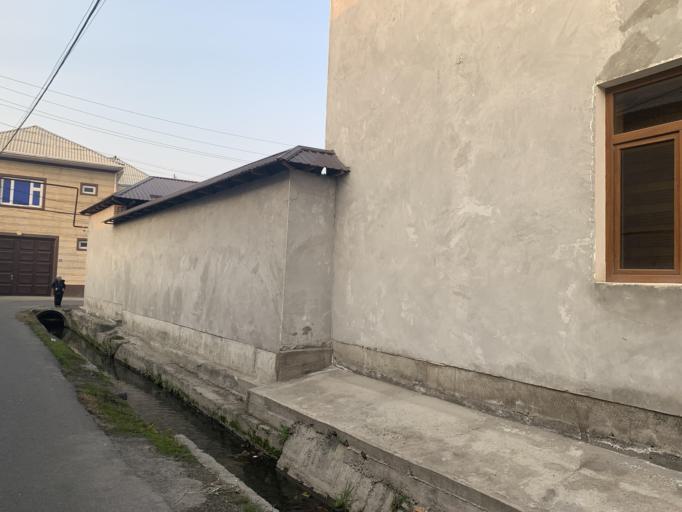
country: UZ
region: Fergana
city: Qo`qon
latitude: 40.5350
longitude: 70.9309
